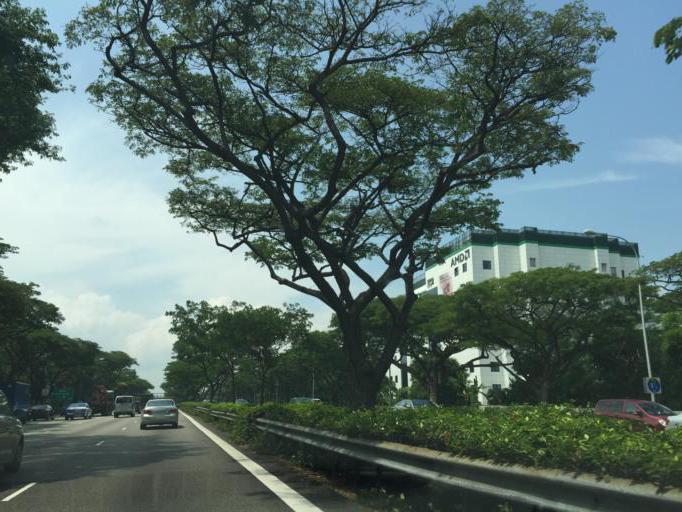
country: SG
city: Singapore
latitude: 1.3302
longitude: 103.9148
